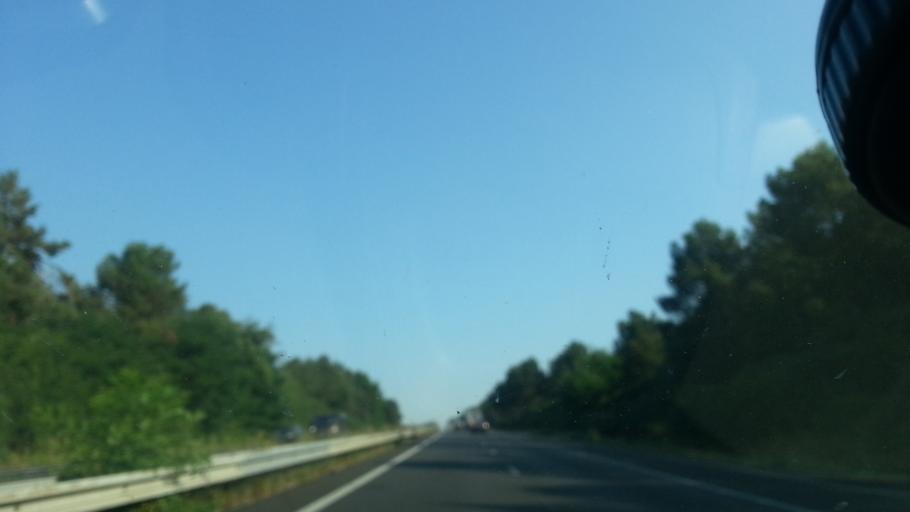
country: FR
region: Poitou-Charentes
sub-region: Departement de la Vienne
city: Dange-Saint-Romain
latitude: 46.9581
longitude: 0.5493
